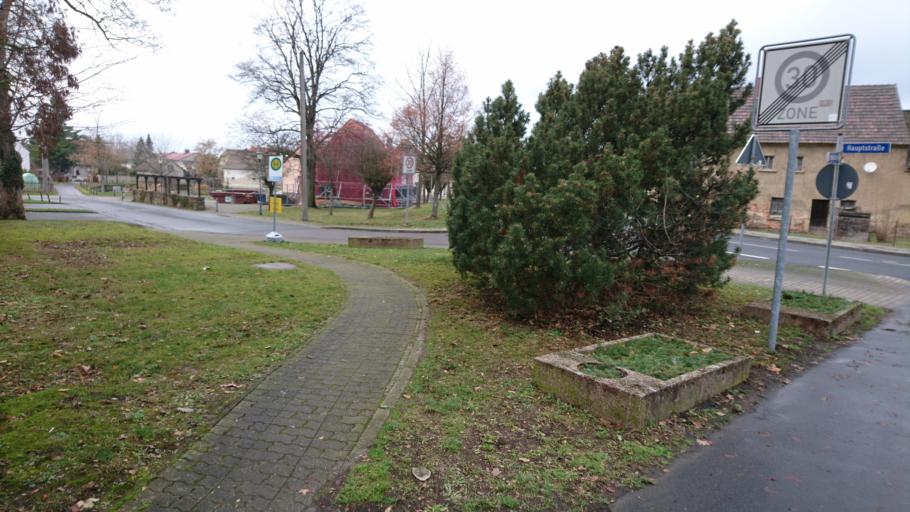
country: DE
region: Saxony
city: Otterwisch
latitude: 51.2379
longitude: 12.6142
